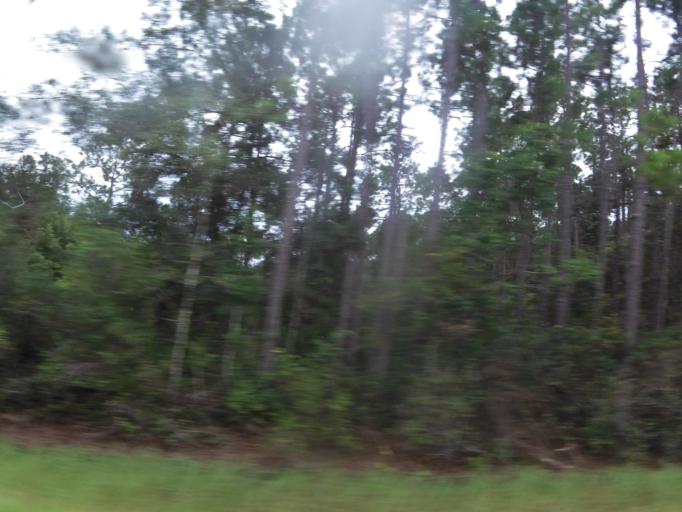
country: US
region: Florida
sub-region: Baker County
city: Macclenny
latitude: 30.5175
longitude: -82.0988
